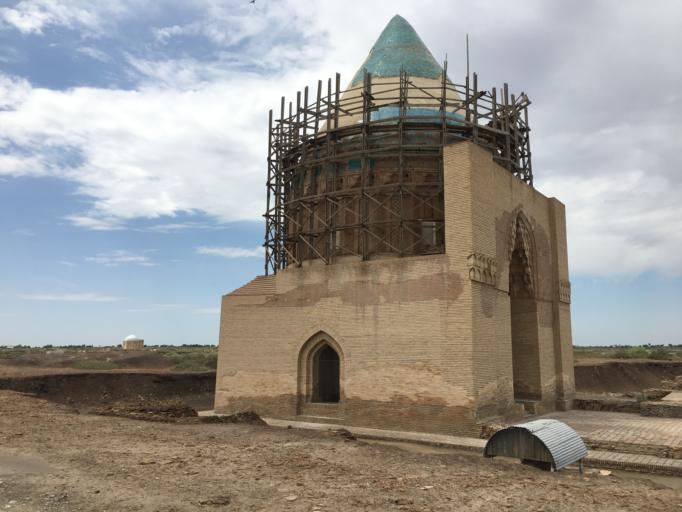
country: TM
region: Dasoguz
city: Koeneuergench
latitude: 42.3076
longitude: 59.1443
